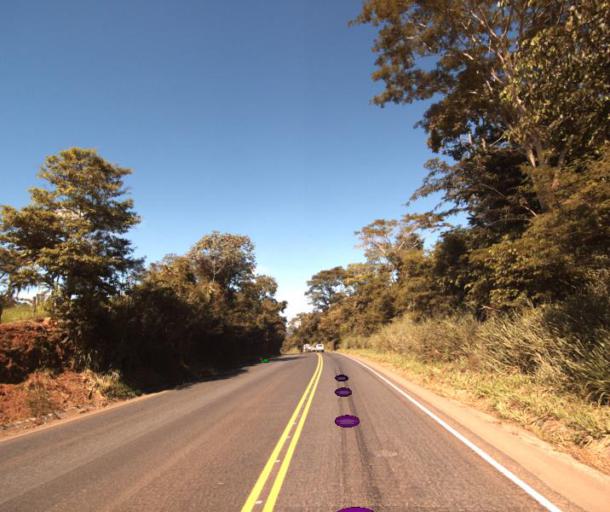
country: BR
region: Goias
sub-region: Ceres
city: Ceres
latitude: -15.1507
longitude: -49.5358
